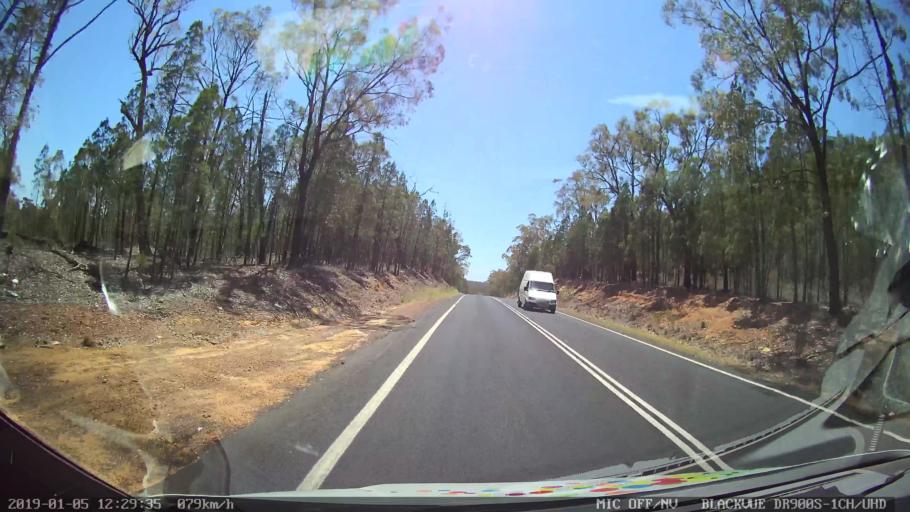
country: AU
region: New South Wales
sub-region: Warrumbungle Shire
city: Coonabarabran
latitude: -31.2323
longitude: 149.3390
